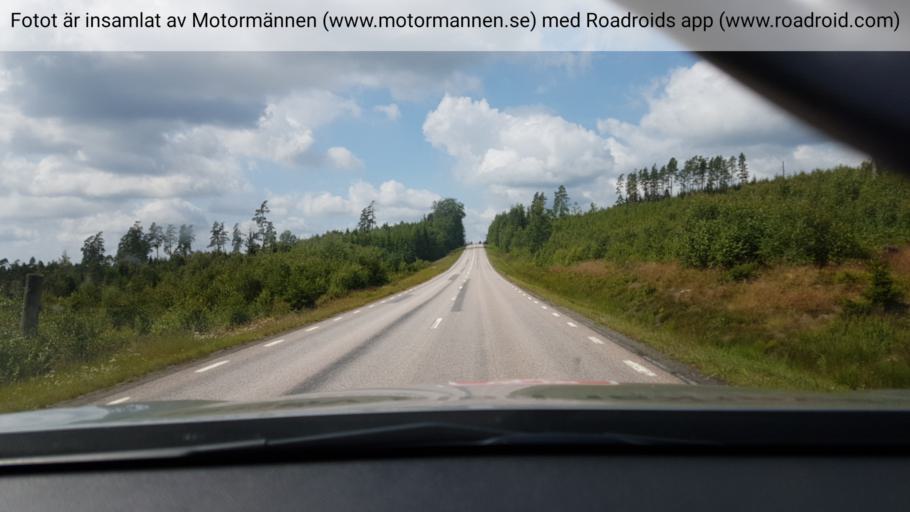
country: SE
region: Vaestra Goetaland
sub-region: Svenljunga Kommun
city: Svenljunga
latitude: 57.4841
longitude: 13.0086
